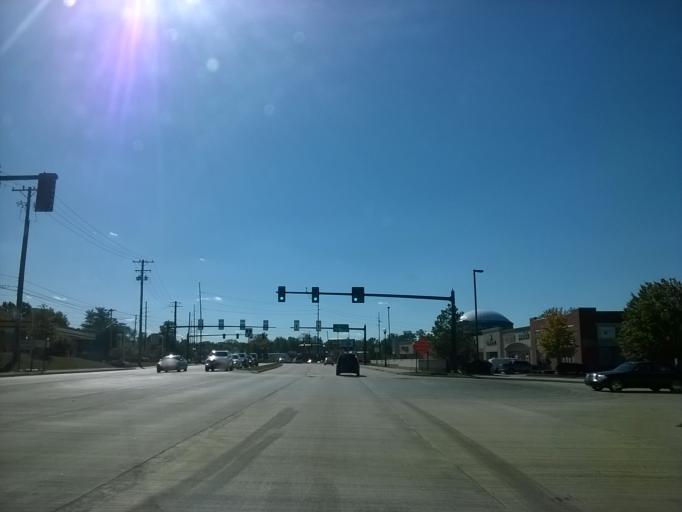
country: US
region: Indiana
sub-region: Hamilton County
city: Fishers
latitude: 39.9284
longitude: -86.0644
